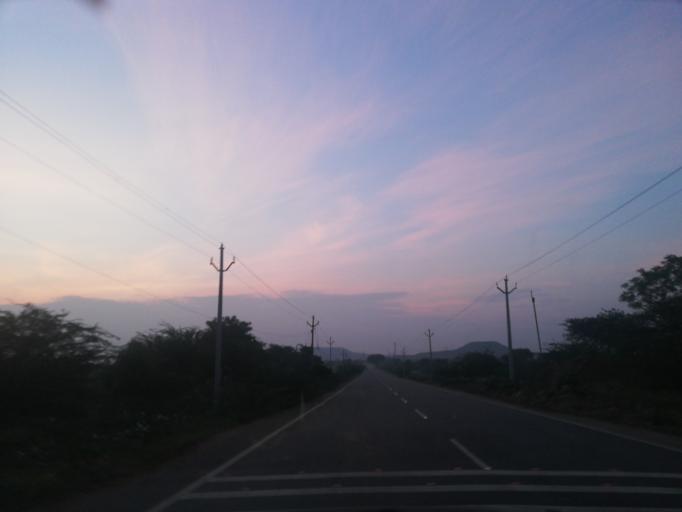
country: IN
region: Andhra Pradesh
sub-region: Guntur
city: Macherla
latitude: 16.6824
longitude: 79.2585
